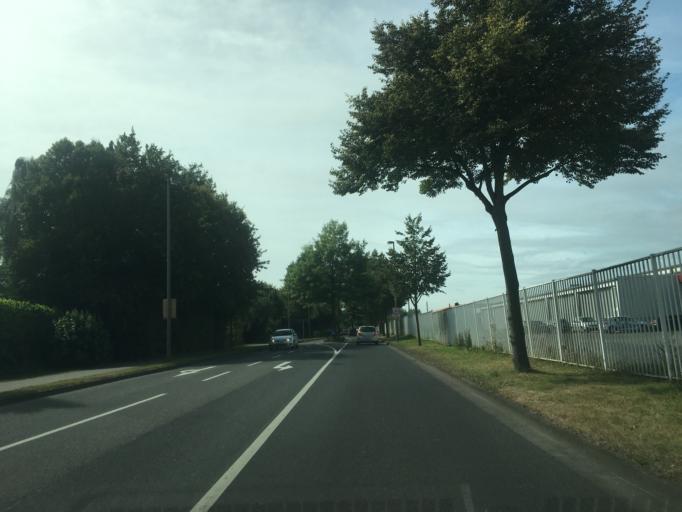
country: DE
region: North Rhine-Westphalia
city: Erkelenz
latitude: 51.0727
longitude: 6.3055
